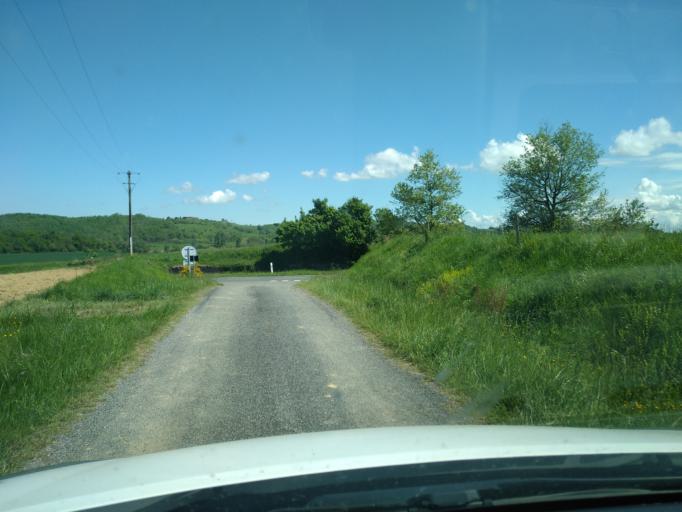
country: FR
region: Midi-Pyrenees
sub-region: Departement de la Haute-Garonne
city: Boulogne-sur-Gesse
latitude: 43.3038
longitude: 0.6742
